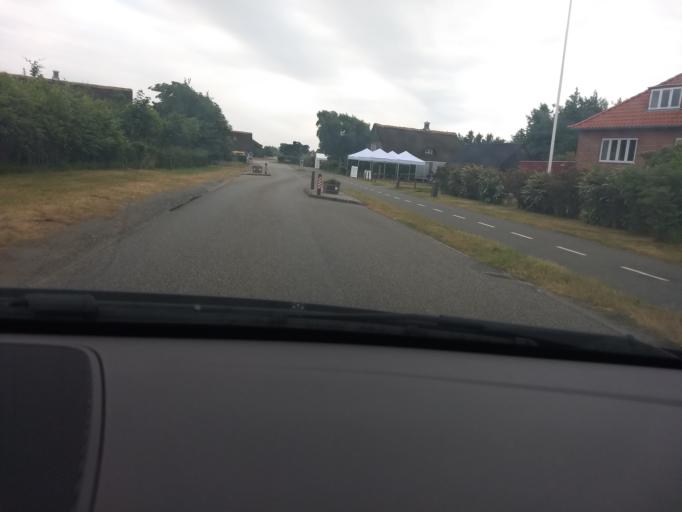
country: DK
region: South Denmark
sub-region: Fano Kommune
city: Nordby
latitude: 55.3511
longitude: 8.4673
